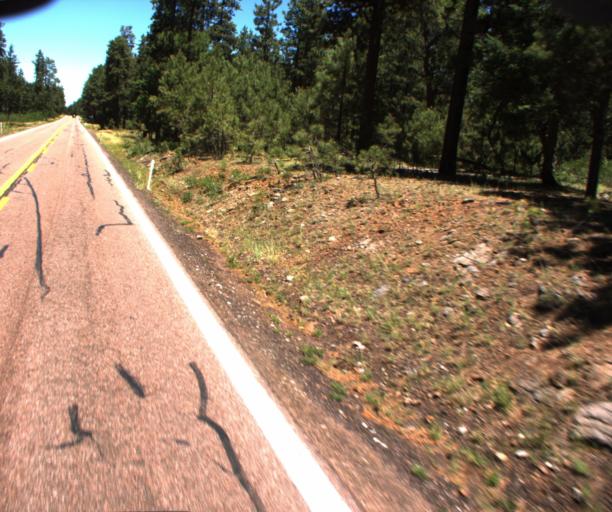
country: US
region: Arizona
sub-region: Gila County
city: Pine
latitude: 34.4665
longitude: -111.3829
